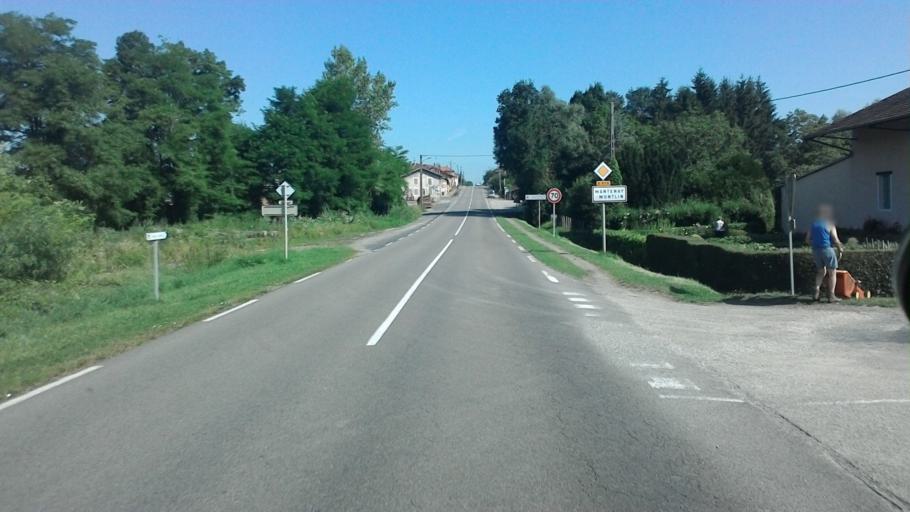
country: FR
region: Rhone-Alpes
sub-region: Departement de l'Ain
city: Saint-Trivier-de-Courtes
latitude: 46.4220
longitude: 5.1000
